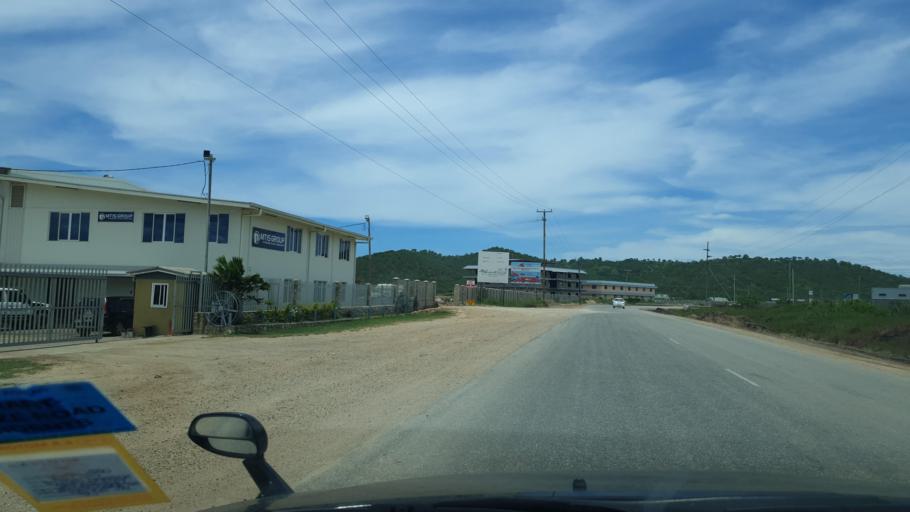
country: PG
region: National Capital
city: Port Moresby
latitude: -9.4198
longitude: 147.0820
